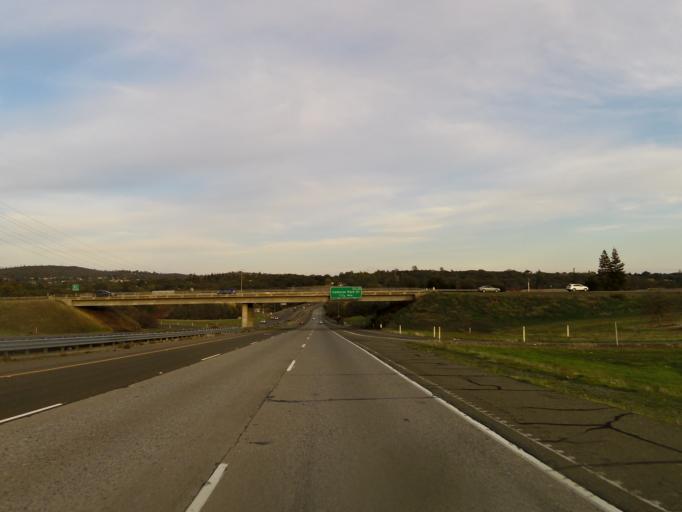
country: US
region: California
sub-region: El Dorado County
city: Cameron Park
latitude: 38.6563
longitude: -120.9996
